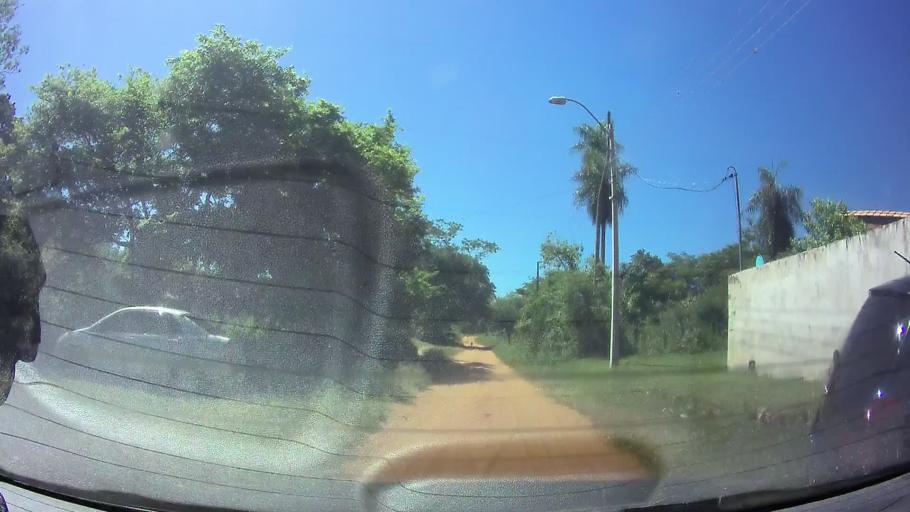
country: PY
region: Central
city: Aregua
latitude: -25.3311
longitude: -57.3970
